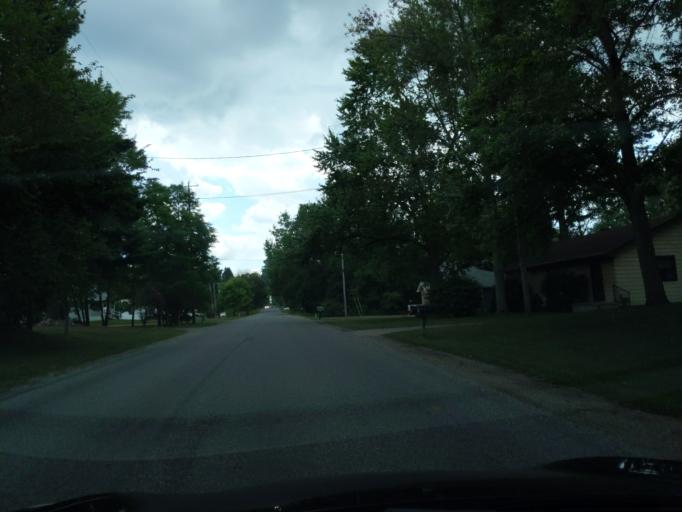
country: US
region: Michigan
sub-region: Ingham County
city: Holt
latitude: 42.6479
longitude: -84.5431
